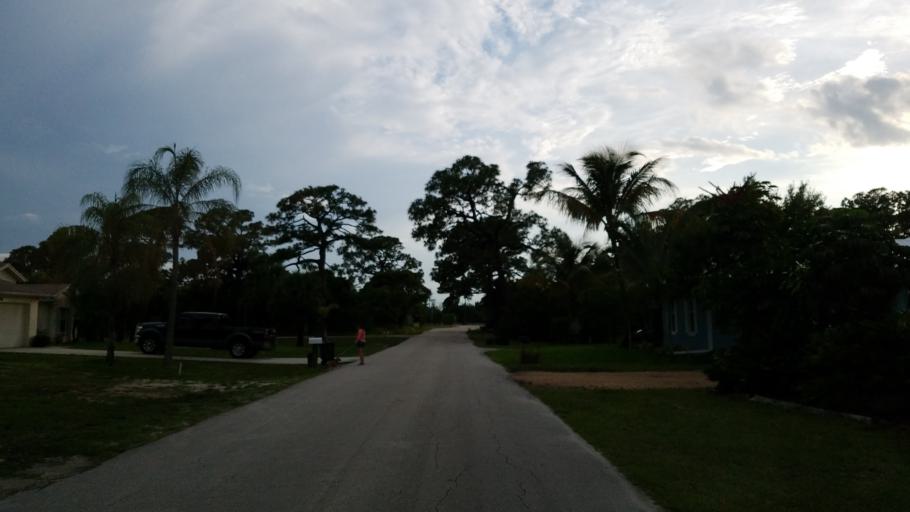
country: US
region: Florida
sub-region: Martin County
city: Port Salerno
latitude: 27.1491
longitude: -80.1984
